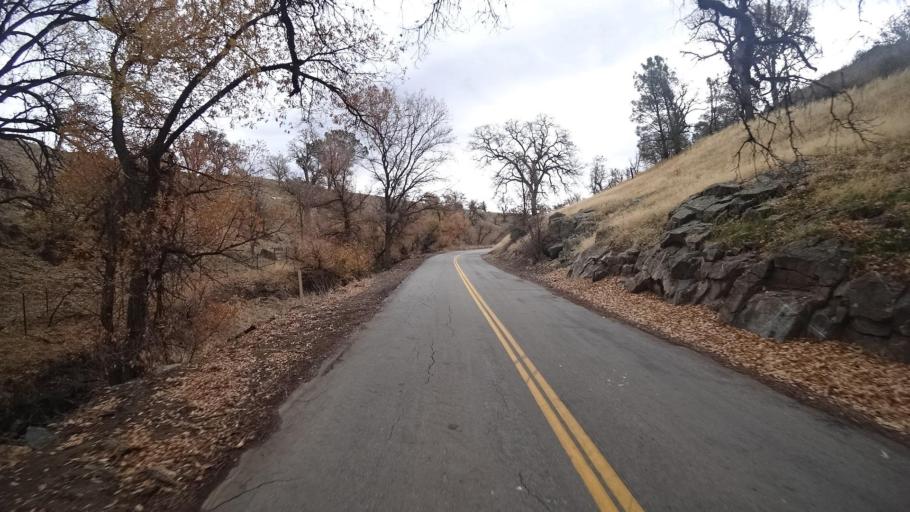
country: US
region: California
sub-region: Kern County
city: Golden Hills
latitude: 35.1291
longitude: -118.5565
